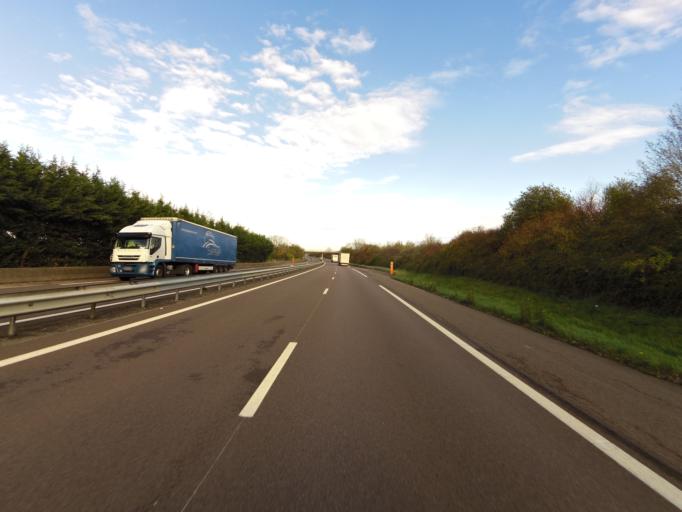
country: FR
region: Bourgogne
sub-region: Departement de la Cote-d'Or
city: Neuilly-les-Dijon
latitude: 47.2465
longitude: 5.1050
